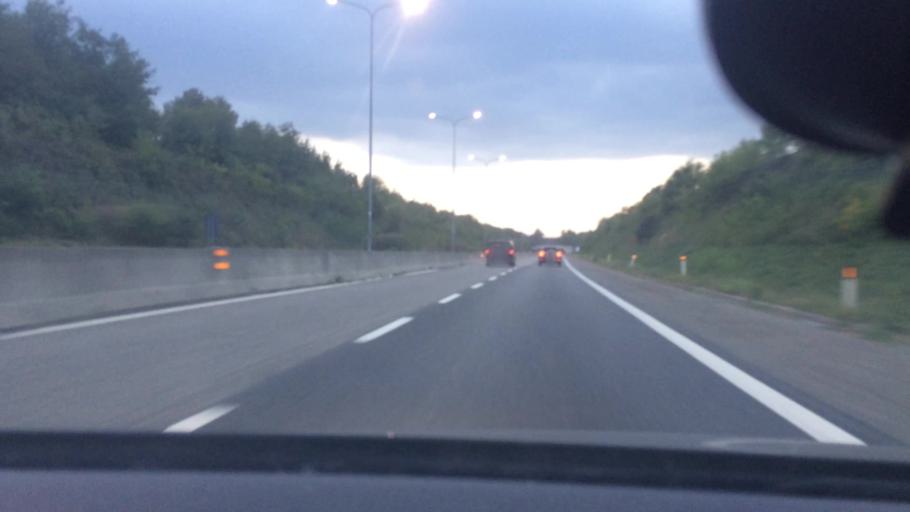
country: IT
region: Lombardy
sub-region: Provincia di Varese
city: Vizzola Ticino
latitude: 45.5992
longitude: 8.7131
